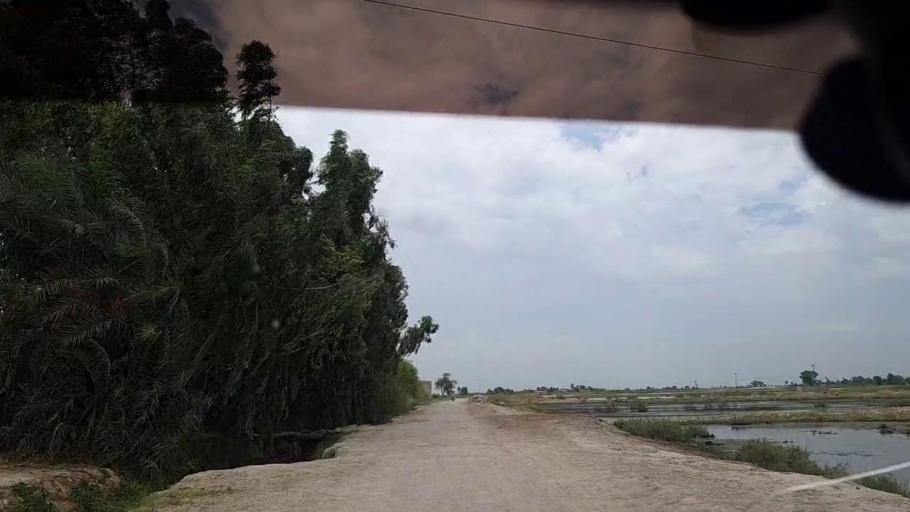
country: PK
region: Sindh
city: Ghauspur
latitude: 28.1113
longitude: 68.9859
